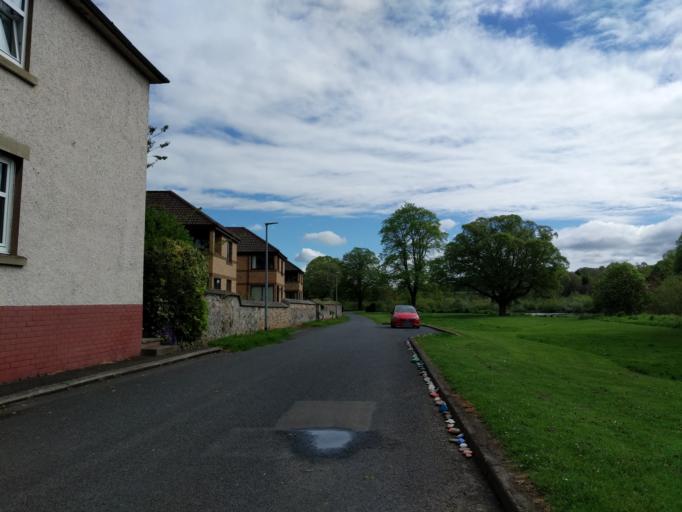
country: GB
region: Scotland
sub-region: The Scottish Borders
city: Kelso
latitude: 55.5958
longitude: -2.4286
